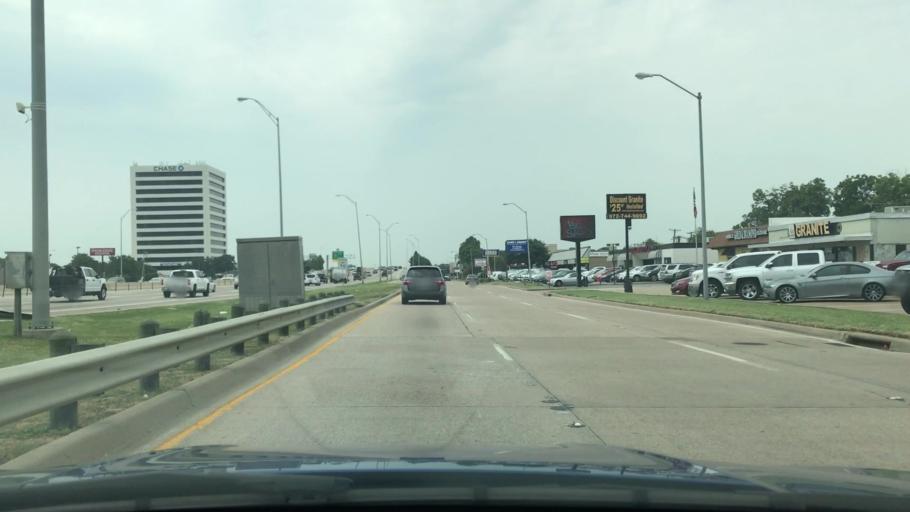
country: US
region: Texas
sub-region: Dallas County
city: Richardson
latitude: 32.9554
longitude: -96.7322
